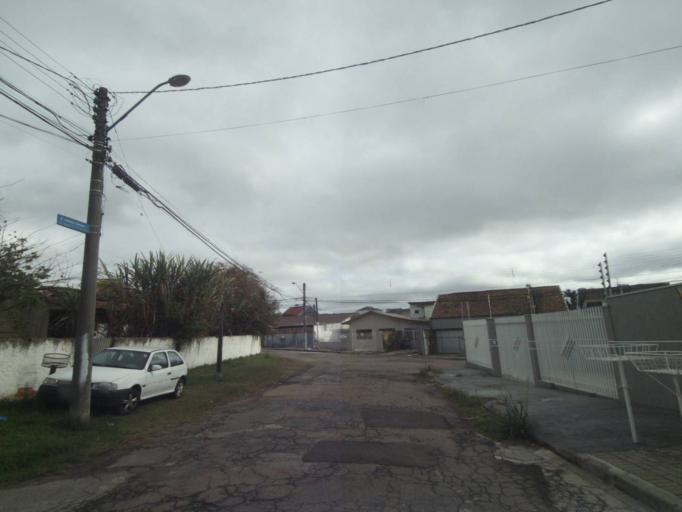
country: BR
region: Parana
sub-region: Curitiba
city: Curitiba
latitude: -25.4992
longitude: -49.2848
